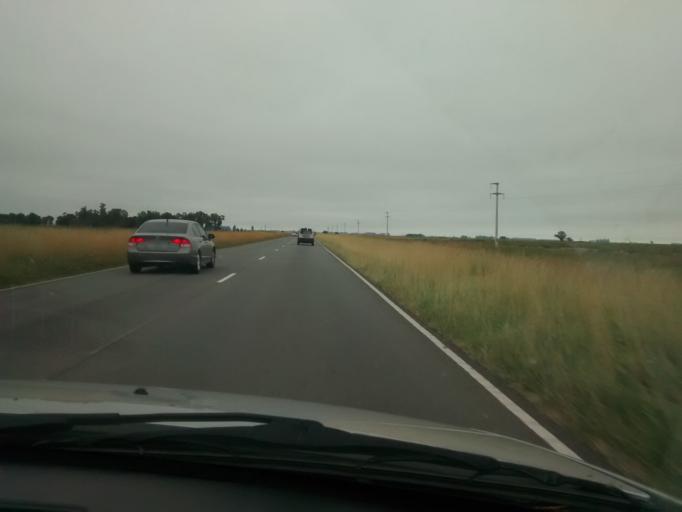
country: AR
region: Buenos Aires
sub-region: Partido de Ayacucho
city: Ayacucho
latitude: -37.0515
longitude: -58.5422
